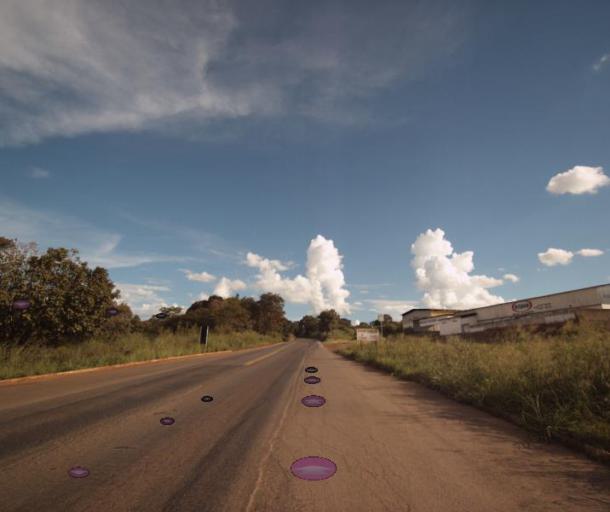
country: BR
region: Goias
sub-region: Rialma
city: Rialma
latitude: -15.3110
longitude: -49.5722
